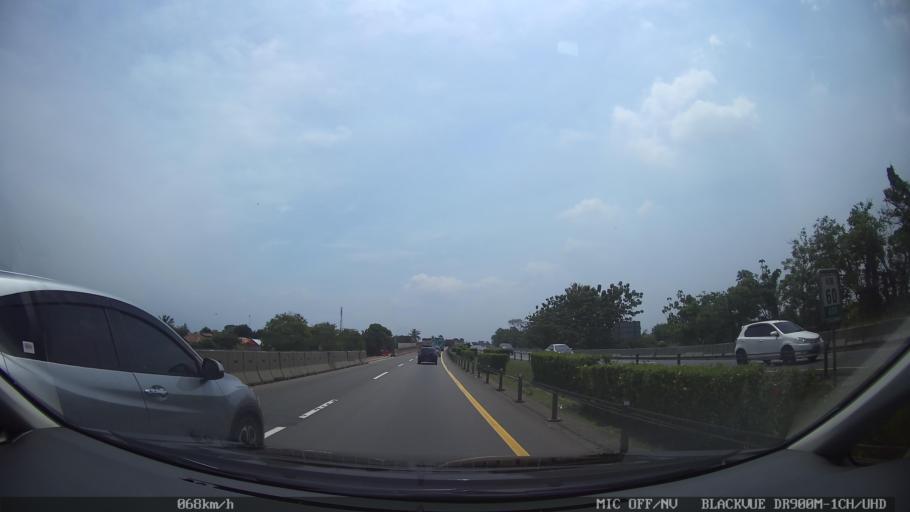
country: ID
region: West Java
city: Kresek
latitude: -6.1436
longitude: 106.2787
